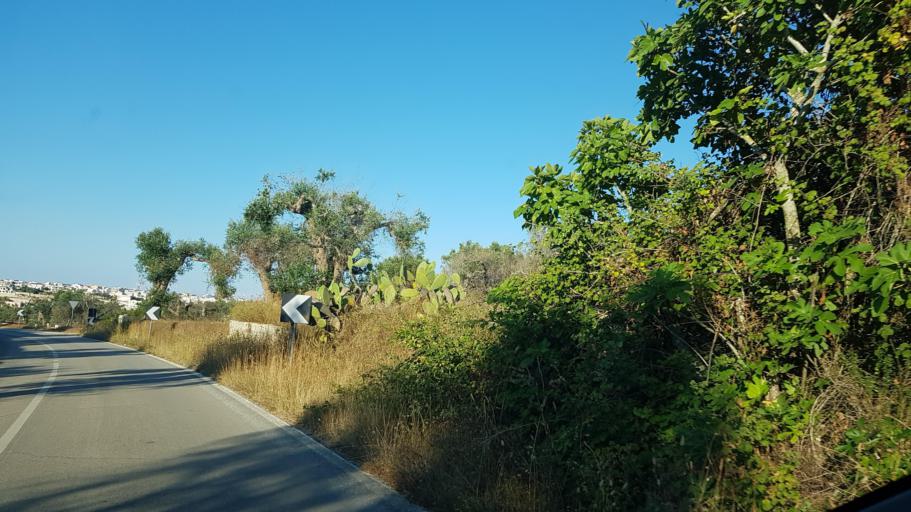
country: IT
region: Apulia
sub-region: Provincia di Lecce
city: Castro
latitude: 40.0027
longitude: 18.4132
